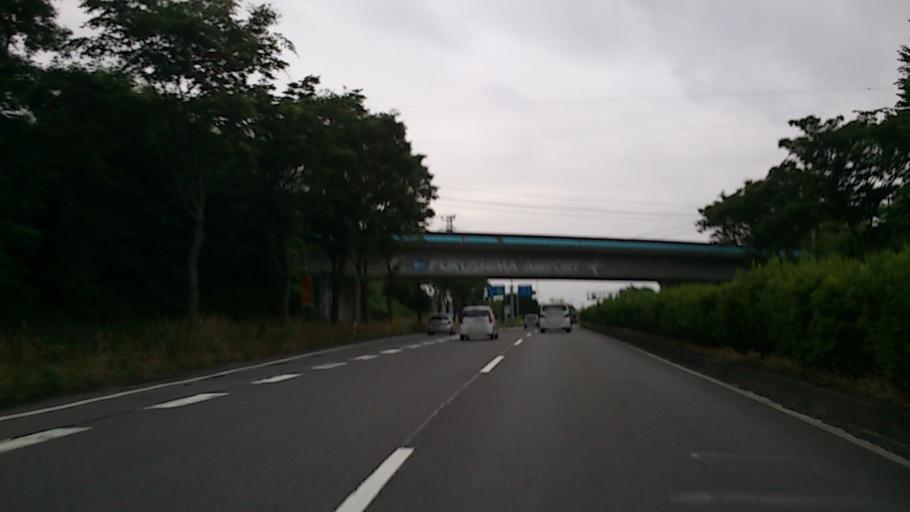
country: JP
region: Fukushima
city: Sukagawa
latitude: 37.2787
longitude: 140.3650
